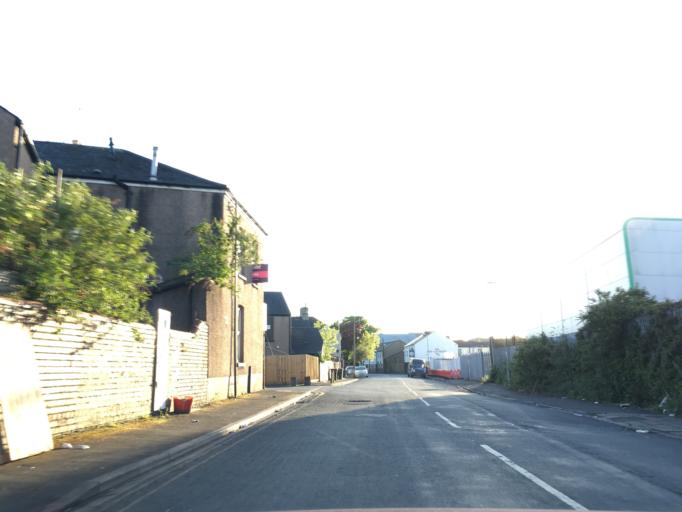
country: GB
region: Wales
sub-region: Newport
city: Newport
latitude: 51.5774
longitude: -2.9848
